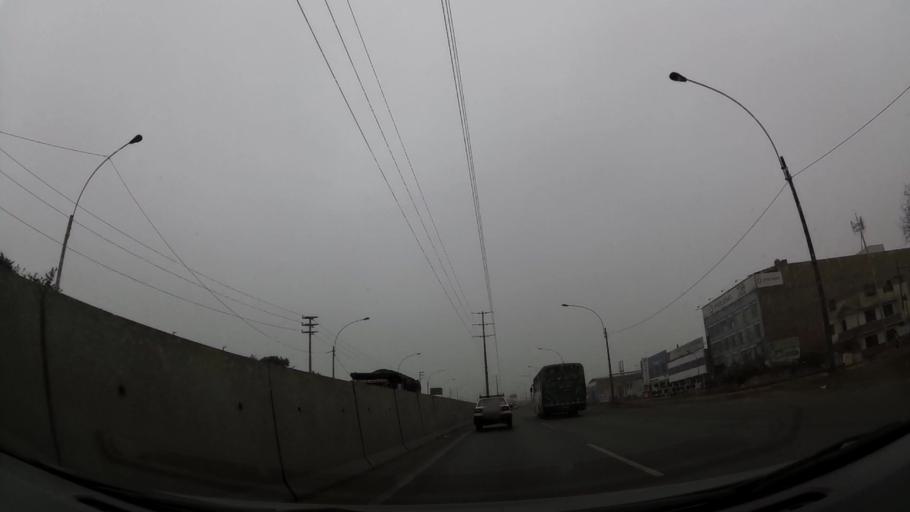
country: PE
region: Lima
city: Ventanilla
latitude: -11.8398
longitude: -77.1056
